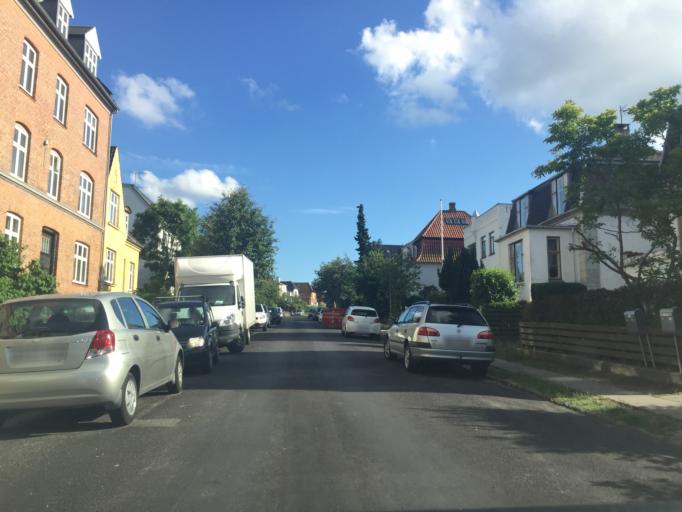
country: DK
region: Capital Region
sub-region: Kobenhavn
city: Vanlose
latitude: 55.7037
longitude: 12.5051
